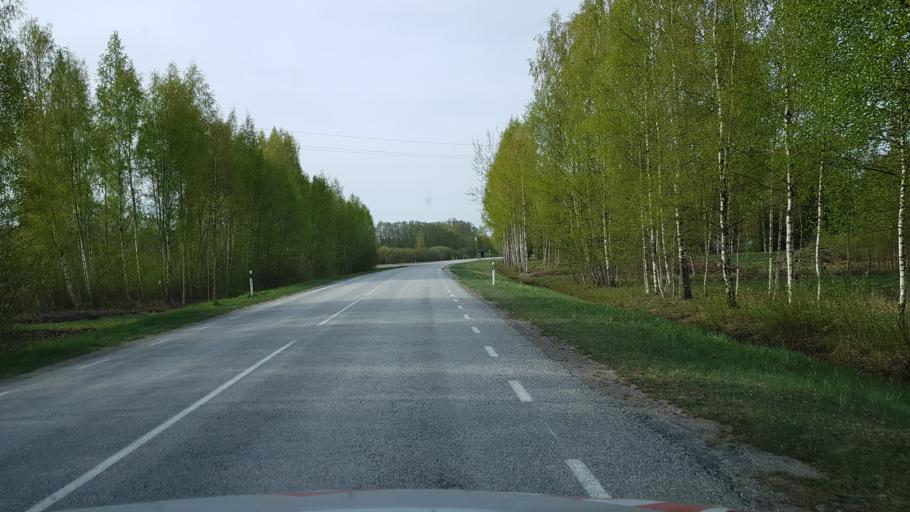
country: EE
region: Paernumaa
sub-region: Audru vald
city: Audru
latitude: 58.4075
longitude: 24.3071
